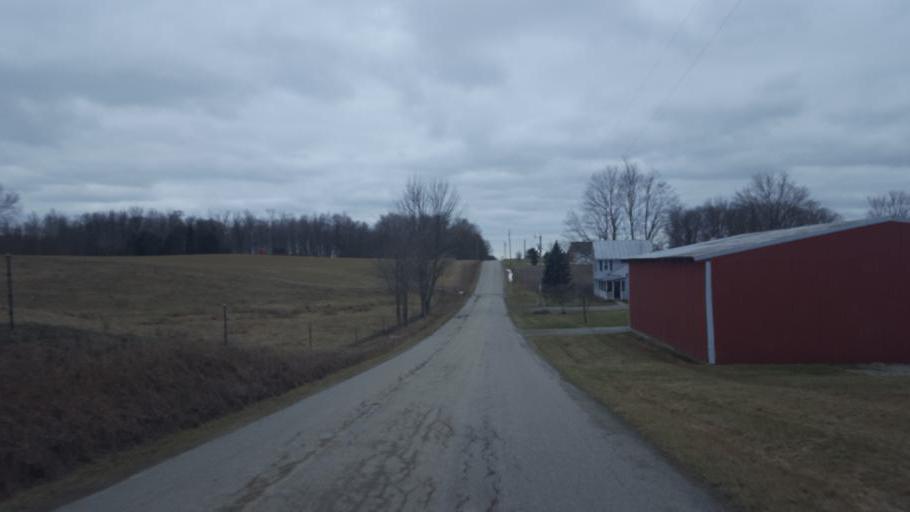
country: US
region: Ohio
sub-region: Morrow County
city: Mount Gilead
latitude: 40.5994
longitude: -82.7477
